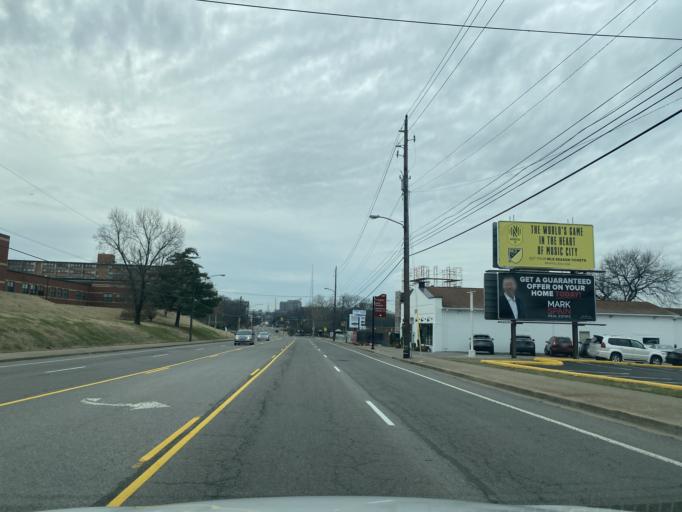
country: US
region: Tennessee
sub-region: Davidson County
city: Nashville
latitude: 36.1443
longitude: -86.7866
